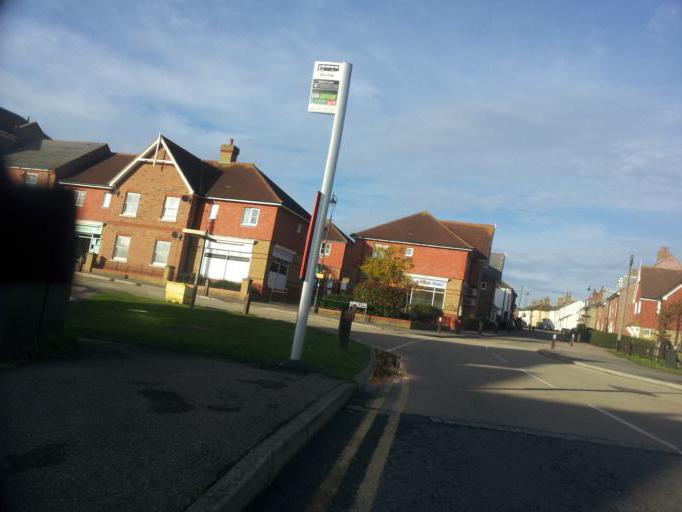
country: GB
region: England
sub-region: Kent
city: Sittingbourne
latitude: 51.3773
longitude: 0.7294
